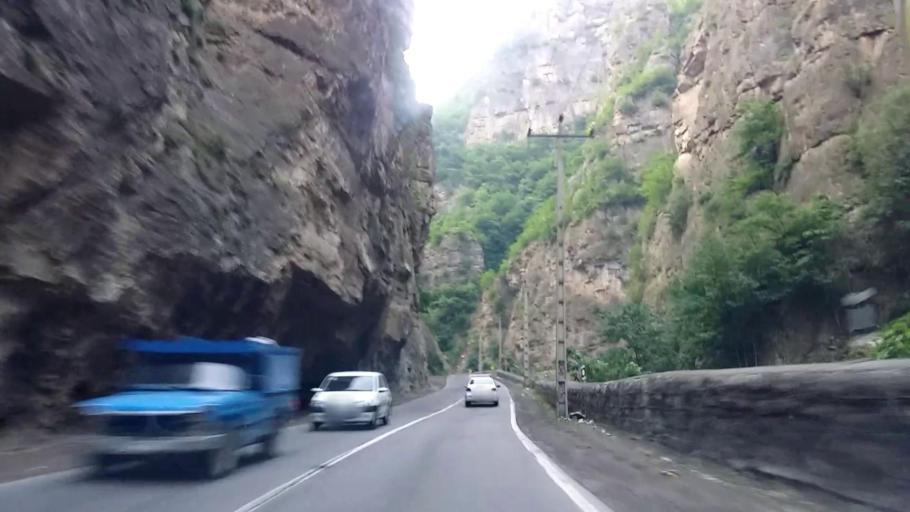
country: IR
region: Mazandaran
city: Chalus
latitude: 36.2727
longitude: 51.2444
